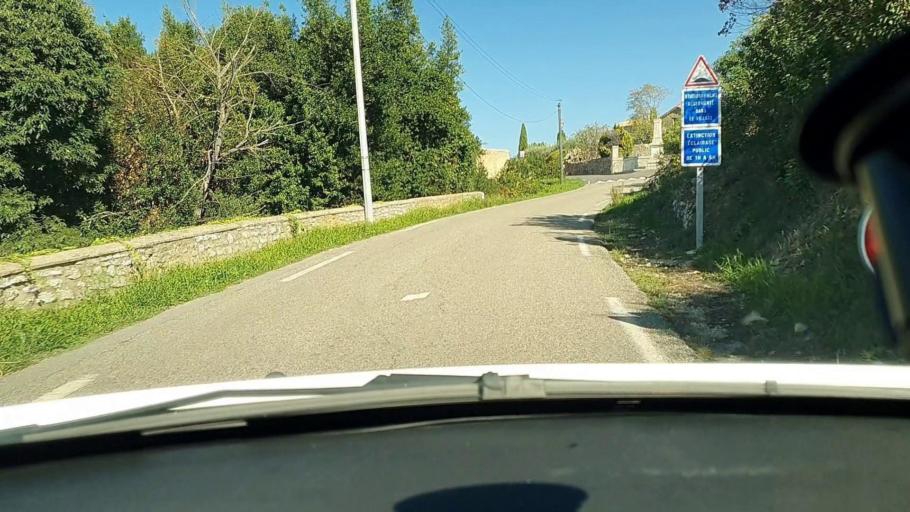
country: FR
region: Languedoc-Roussillon
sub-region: Departement du Gard
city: Saint-Julien-de-Peyrolas
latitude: 44.2592
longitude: 4.5248
